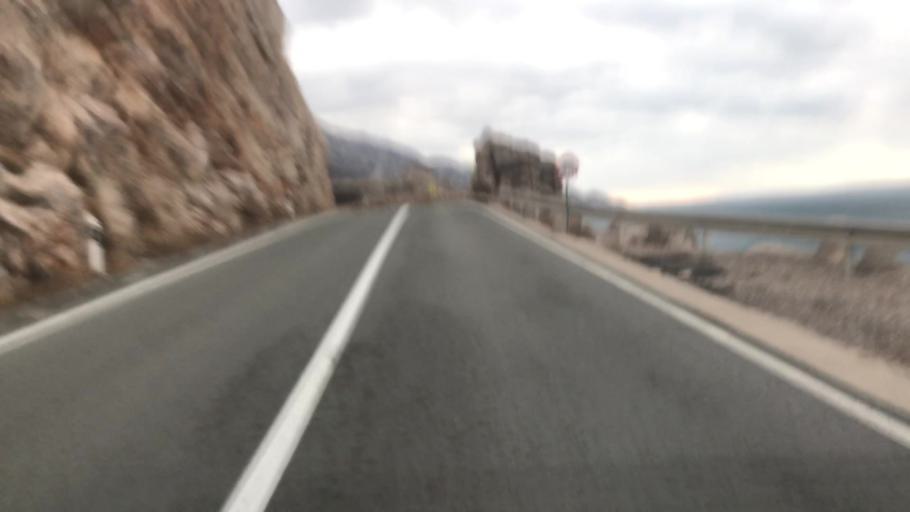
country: HR
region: Licko-Senjska
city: Karlobag
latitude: 44.5173
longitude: 15.0892
